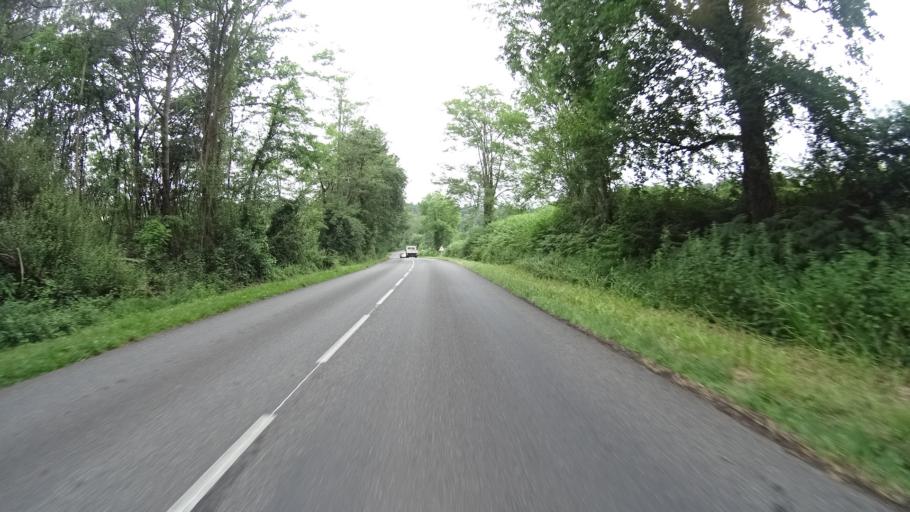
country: FR
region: Aquitaine
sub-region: Departement des Pyrenees-Atlantiques
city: Orthez
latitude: 43.5218
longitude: -0.7773
